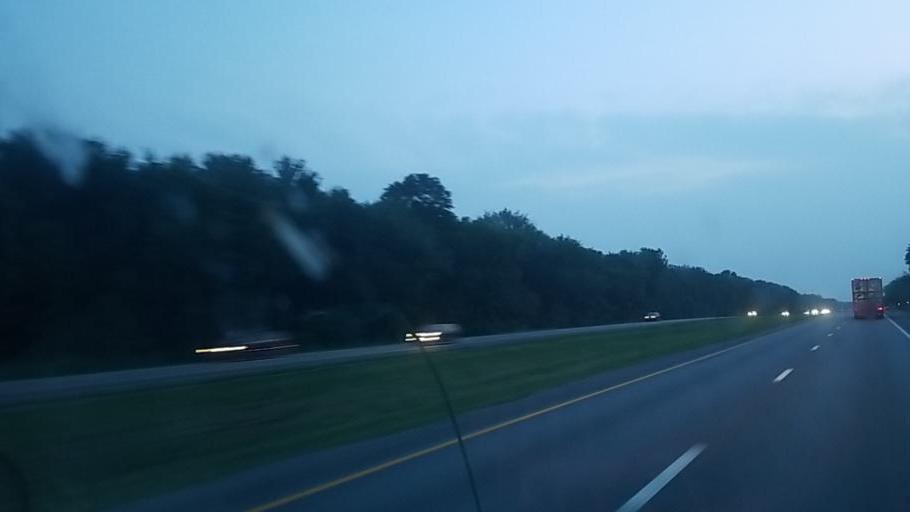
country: US
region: New York
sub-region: Madison County
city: Bolivar
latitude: 43.0947
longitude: -75.8827
